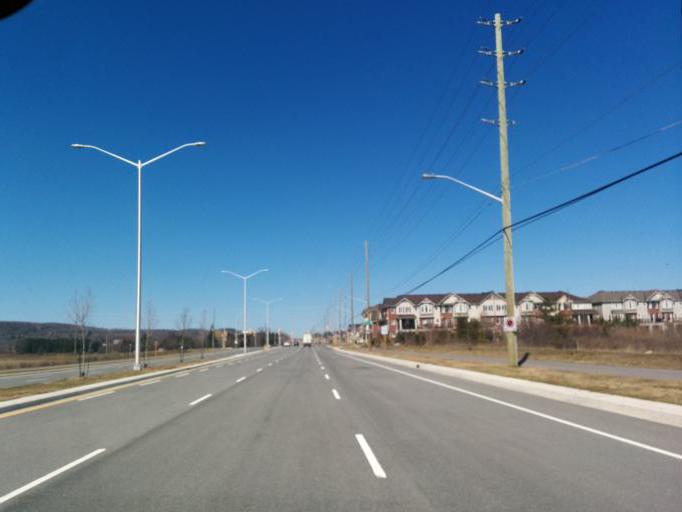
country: CA
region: Ontario
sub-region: Halton
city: Milton
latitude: 43.4846
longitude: -79.8819
